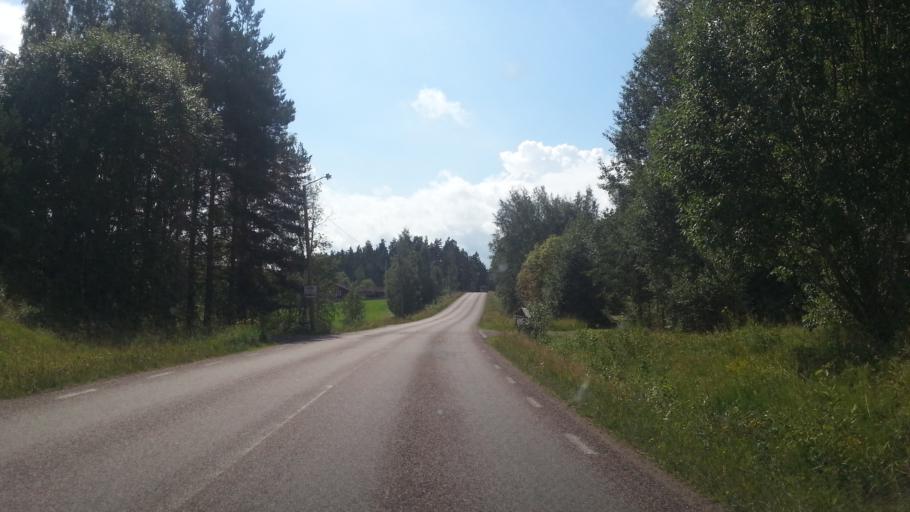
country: SE
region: Dalarna
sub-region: Faluns Kommun
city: Falun
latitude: 60.6209
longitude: 15.7668
